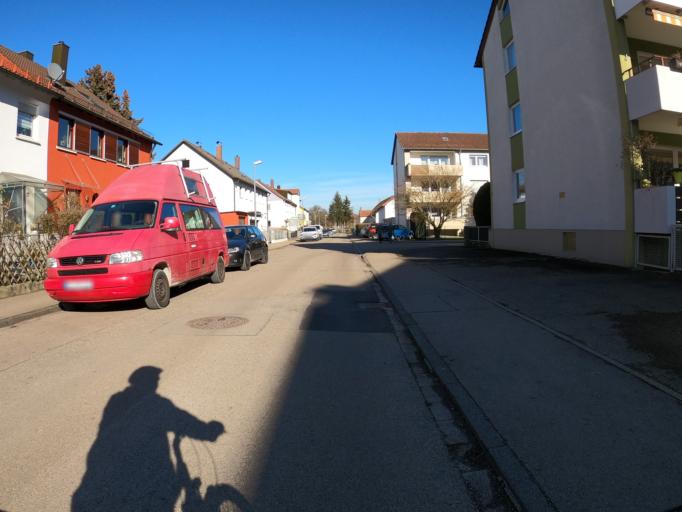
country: DE
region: Bavaria
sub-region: Swabia
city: Neu-Ulm
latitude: 48.4112
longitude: 10.0350
